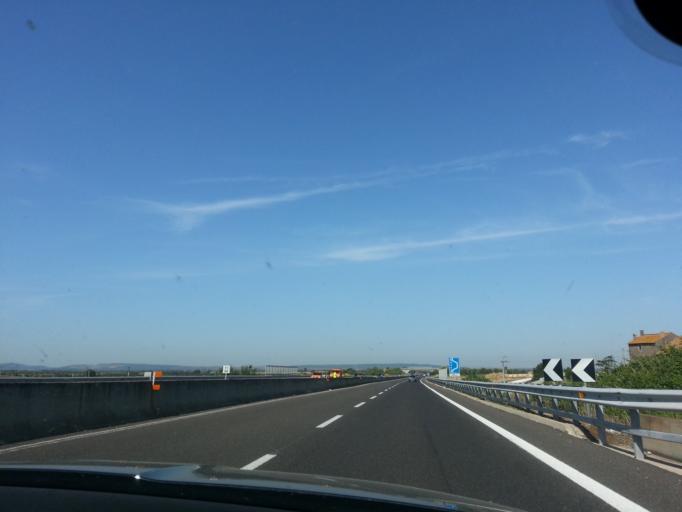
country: IT
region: Latium
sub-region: Provincia di Viterbo
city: Vetralla
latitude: 42.3697
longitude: 12.0349
